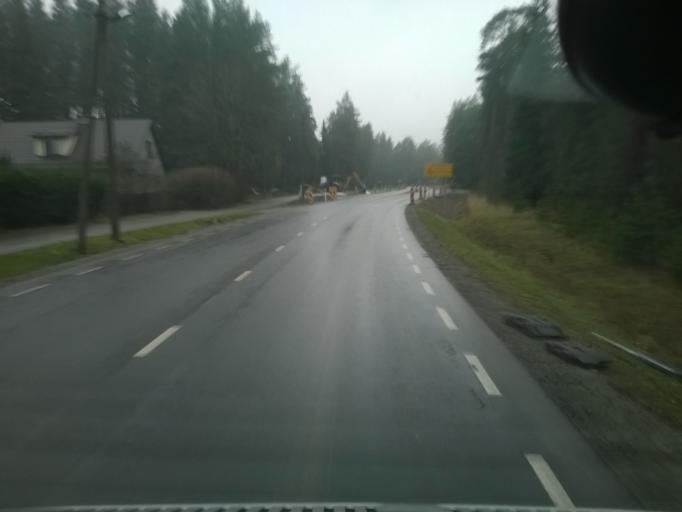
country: EE
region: Harju
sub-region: Saku vald
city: Saku
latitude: 59.2428
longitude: 24.6802
